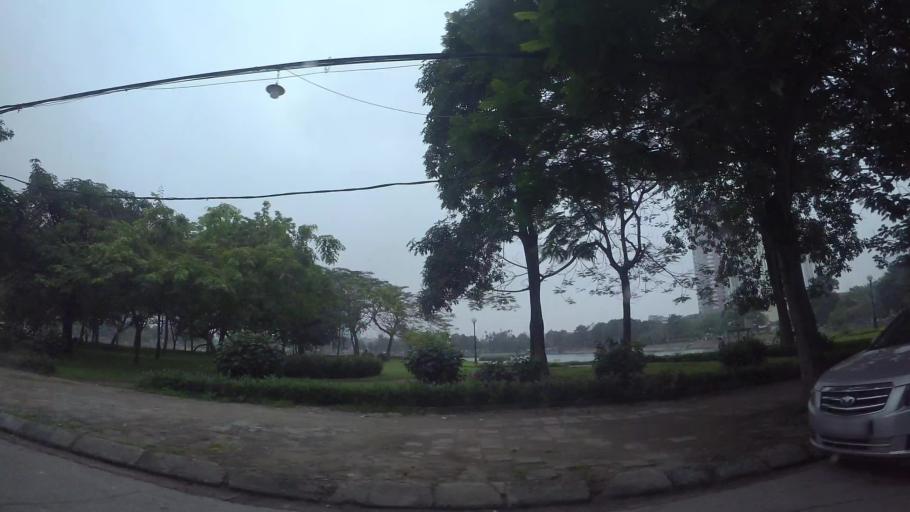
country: VN
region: Ha Noi
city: Hai BaTrung
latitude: 20.9863
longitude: 105.8555
